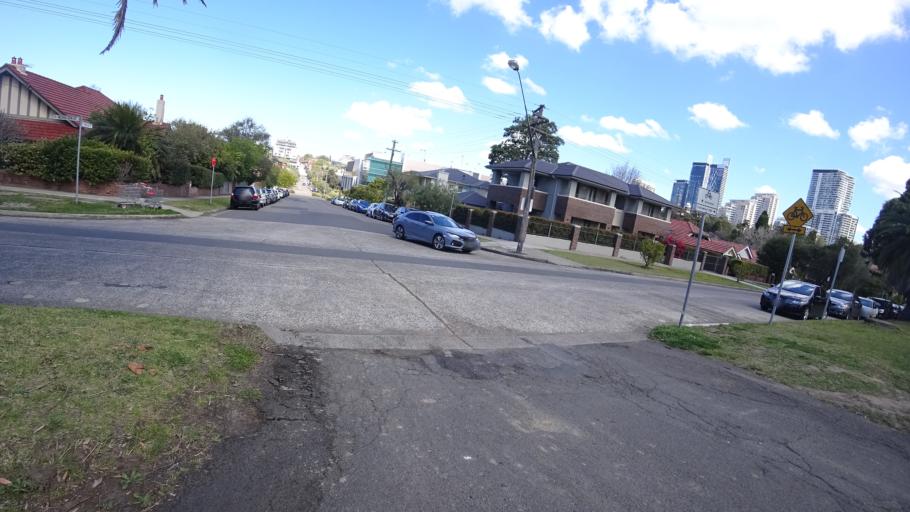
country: AU
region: New South Wales
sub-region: Willoughby
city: Chatswood
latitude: -33.7917
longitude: 151.1863
